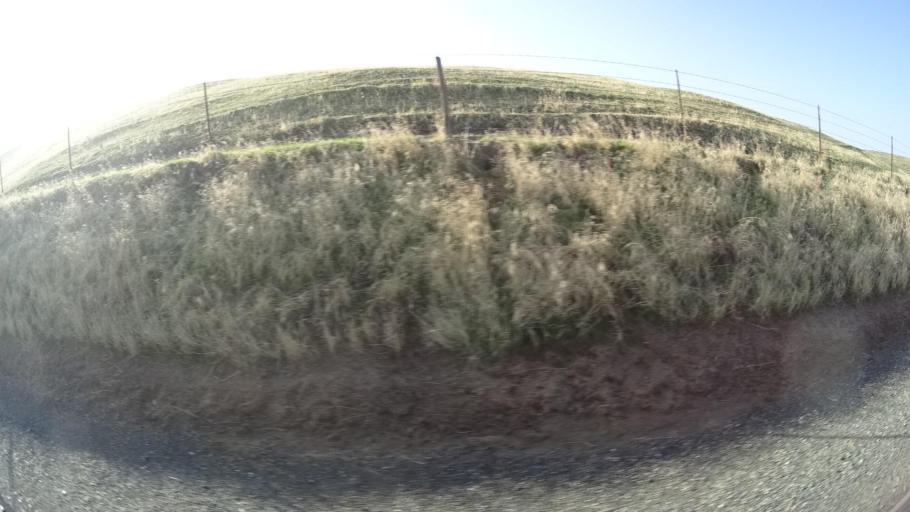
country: US
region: California
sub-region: Tulare County
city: Richgrove
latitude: 35.7489
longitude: -118.9885
